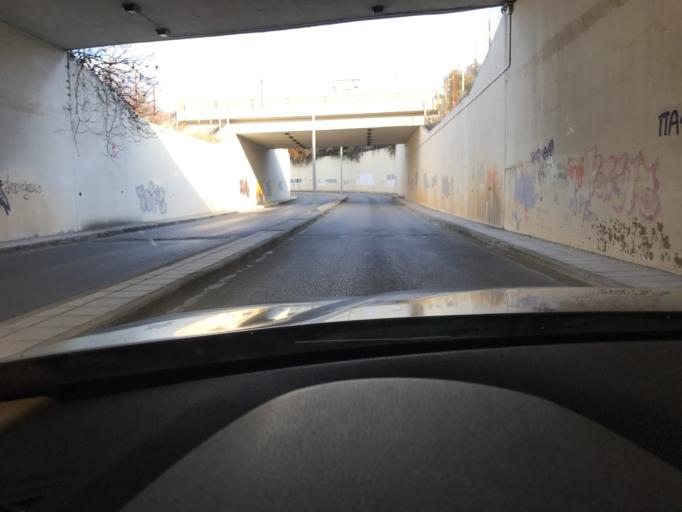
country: GR
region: Central Macedonia
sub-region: Nomos Thessalonikis
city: Efkarpia
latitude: 40.6789
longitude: 22.9564
